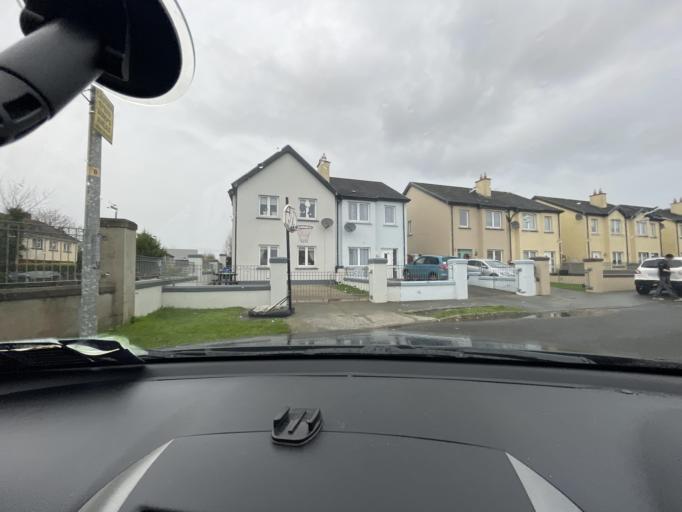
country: IE
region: Ulster
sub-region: An Cabhan
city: Virginia
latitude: 53.8364
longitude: -7.0705
